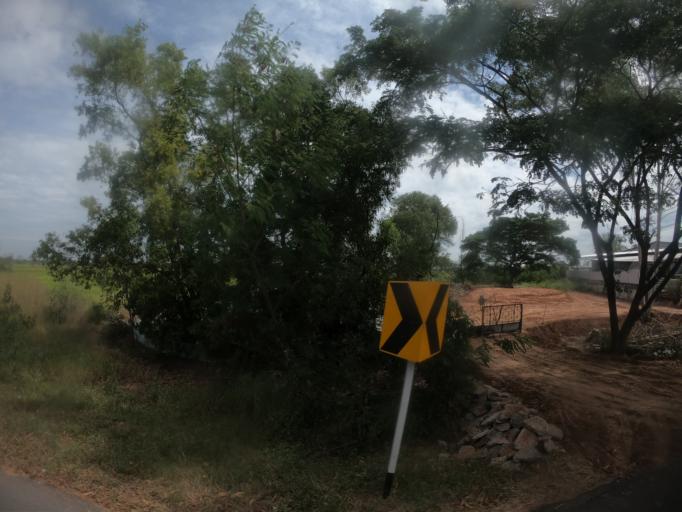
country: TH
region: Maha Sarakham
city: Chiang Yuen
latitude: 16.3708
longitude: 103.1061
